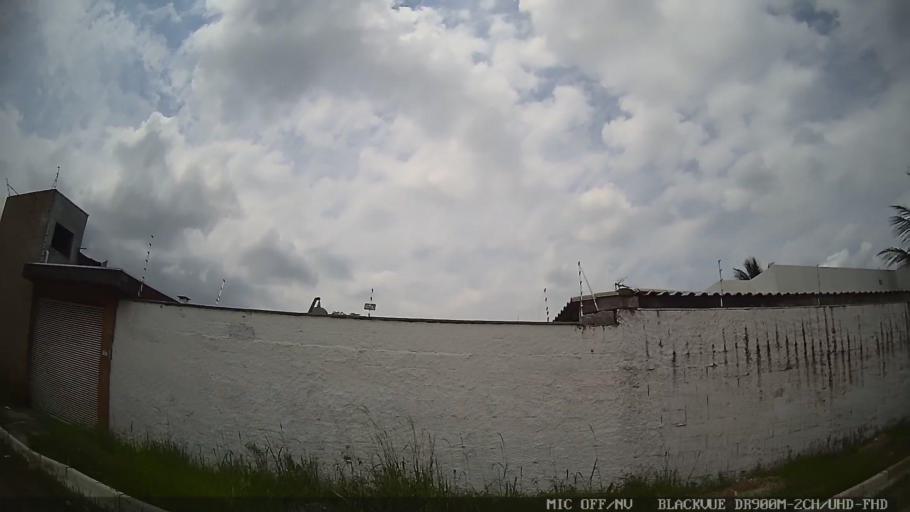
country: BR
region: Sao Paulo
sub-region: Caraguatatuba
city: Caraguatatuba
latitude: -23.6682
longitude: -45.4454
